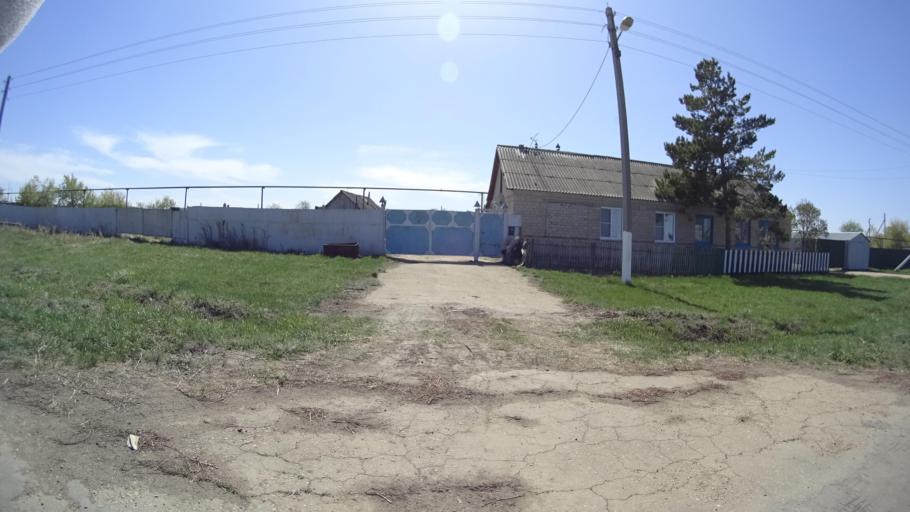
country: RU
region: Chelyabinsk
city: Chesma
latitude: 53.7921
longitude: 61.0385
